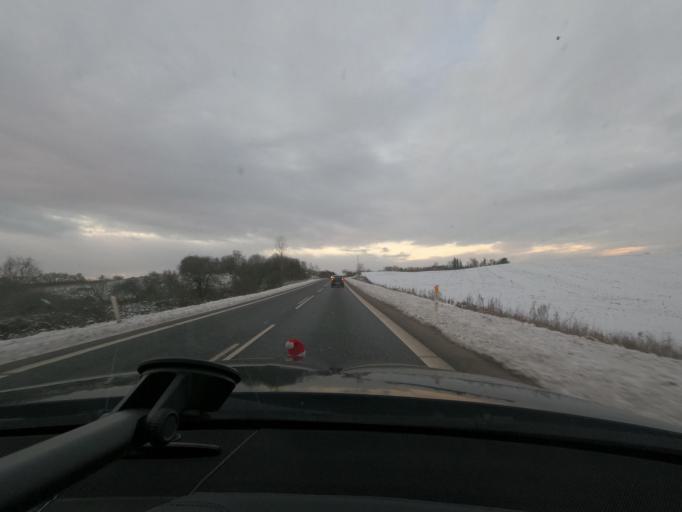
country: DK
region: South Denmark
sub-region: Aabenraa Kommune
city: Krusa
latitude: 54.8646
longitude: 9.4518
